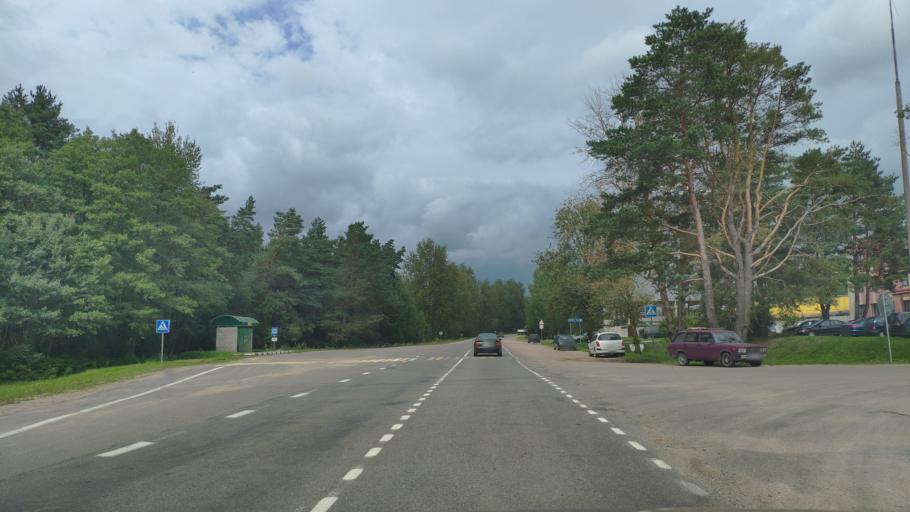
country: BY
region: Minsk
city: Zaslawye
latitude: 53.9857
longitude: 27.2569
